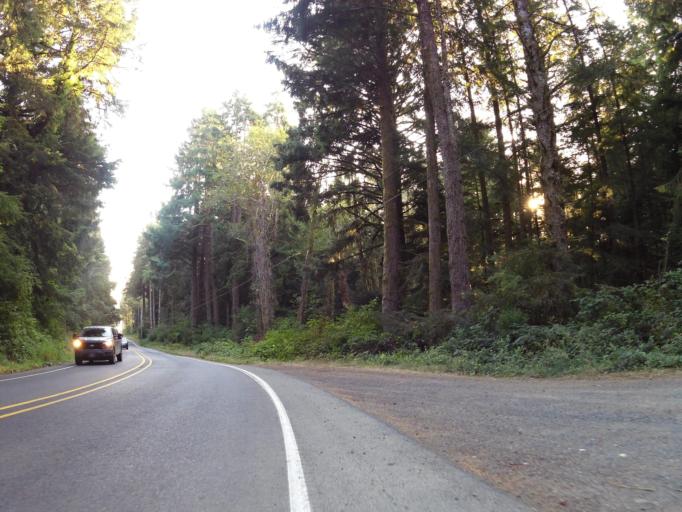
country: US
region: Oregon
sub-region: Lincoln County
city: Lincoln City
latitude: 44.9649
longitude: -123.9971
